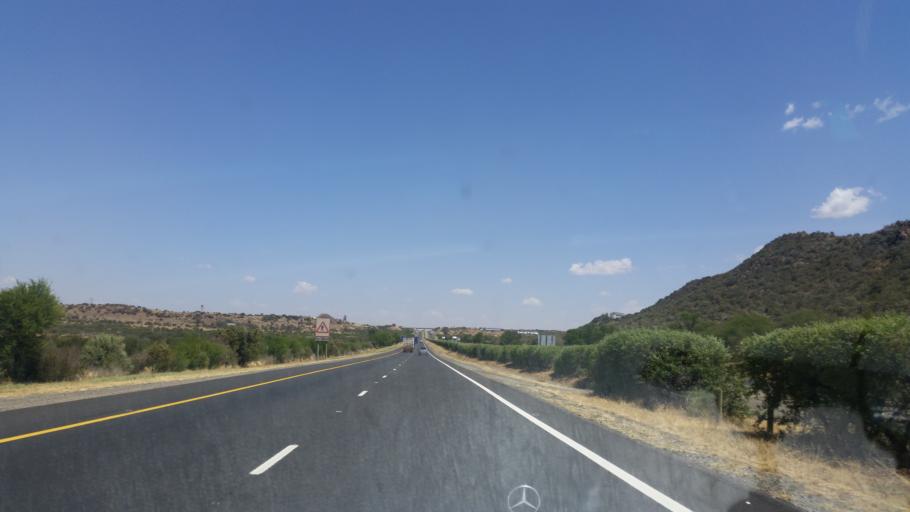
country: ZA
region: Orange Free State
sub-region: Mangaung Metropolitan Municipality
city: Bloemfontein
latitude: -28.9831
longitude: 26.2802
